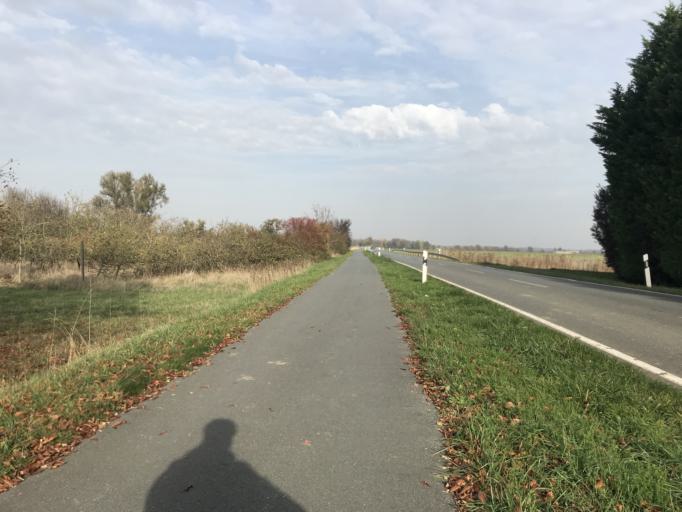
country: DE
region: Hesse
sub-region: Regierungsbezirk Darmstadt
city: Trebur
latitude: 49.9447
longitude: 8.3810
